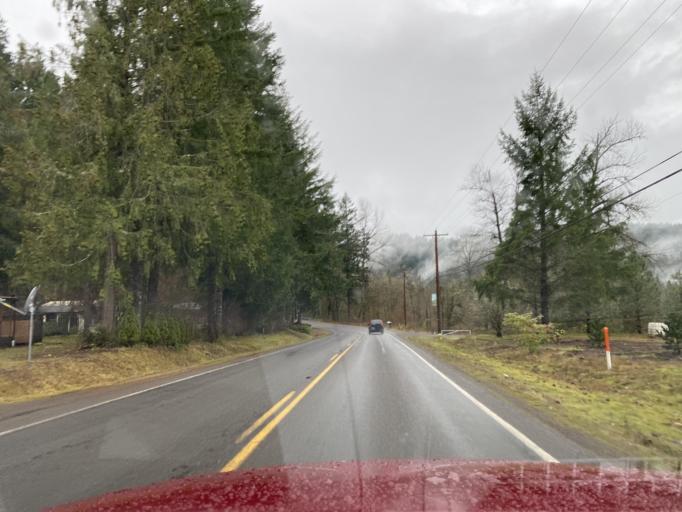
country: US
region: Oregon
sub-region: Lane County
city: Oakridge
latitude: 43.7579
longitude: -122.5220
